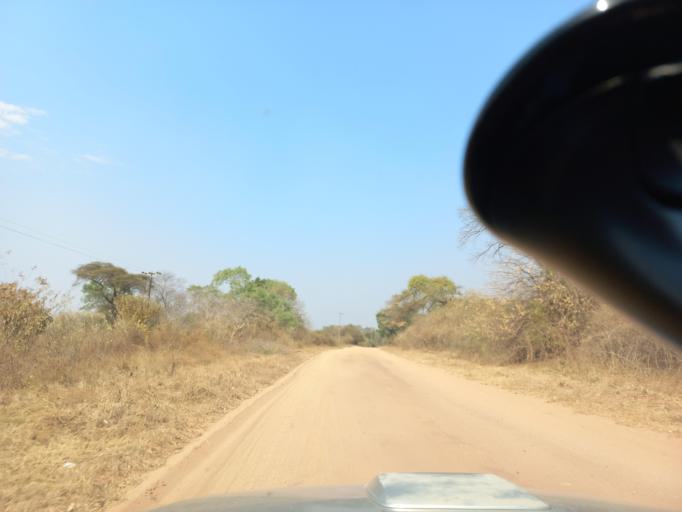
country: ZW
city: Chirundu
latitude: -15.9253
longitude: 28.8777
